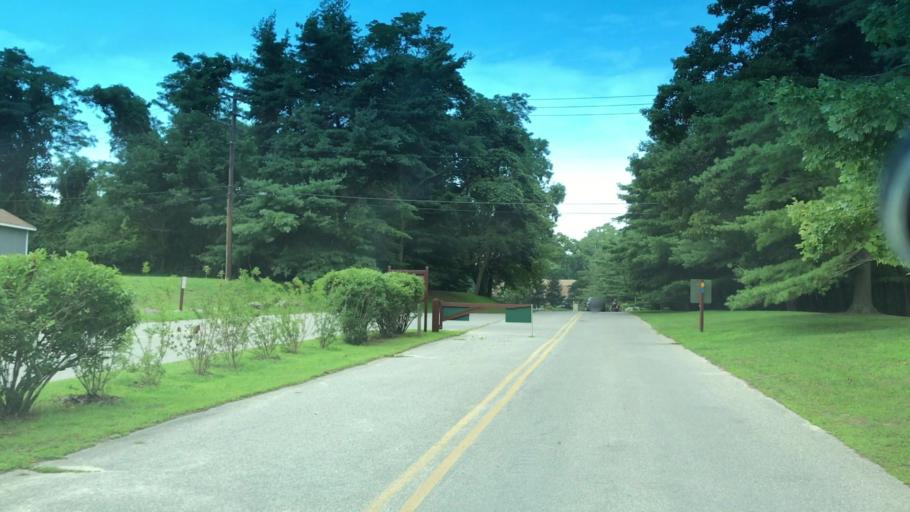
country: US
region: New York
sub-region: Suffolk County
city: Wading River
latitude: 40.9617
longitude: -72.8043
